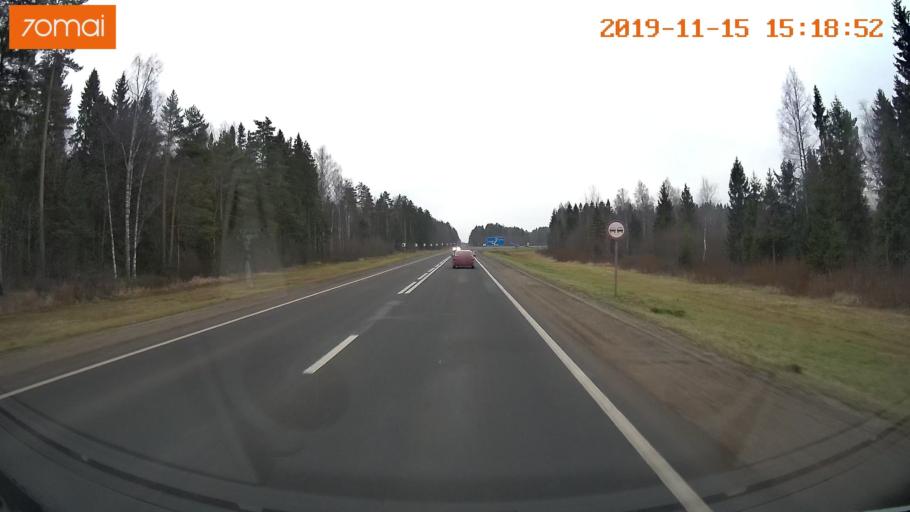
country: RU
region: Jaroslavl
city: Danilov
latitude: 58.2414
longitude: 40.1819
